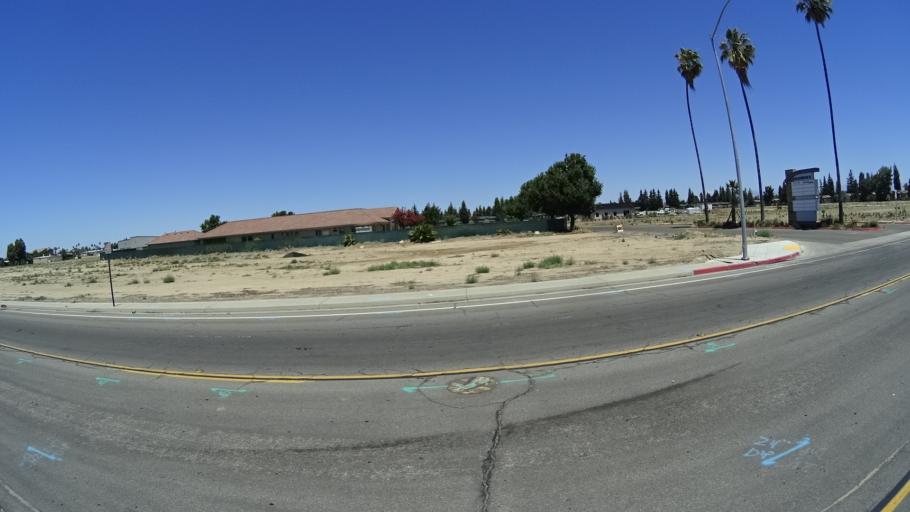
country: US
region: California
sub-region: Fresno County
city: Tarpey Village
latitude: 36.7866
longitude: -119.7226
